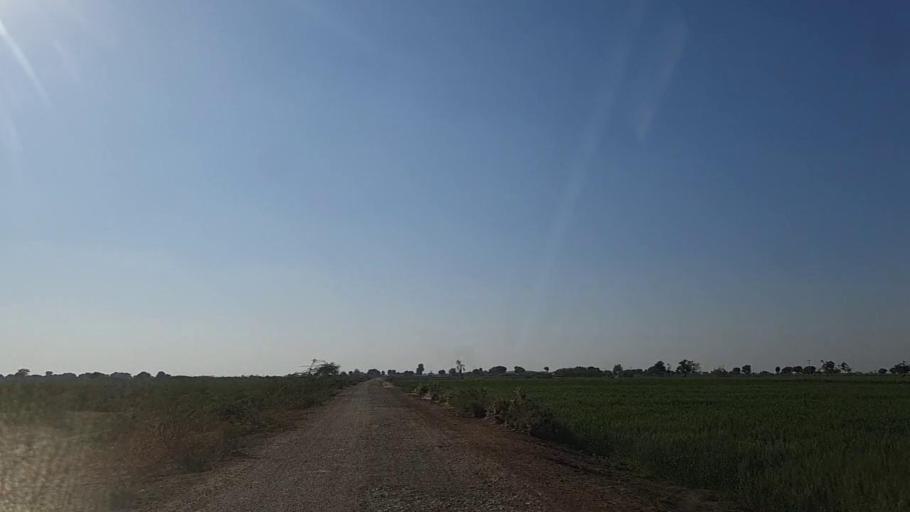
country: PK
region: Sindh
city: Samaro
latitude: 25.3615
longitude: 69.3931
